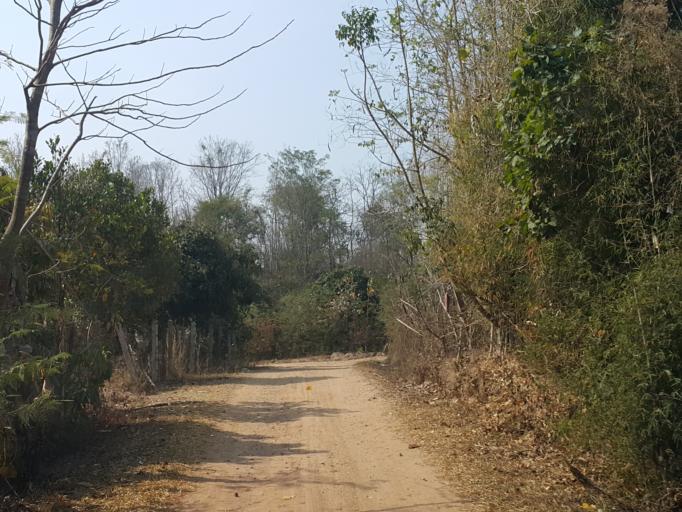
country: TH
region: Chiang Mai
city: Hang Dong
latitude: 18.7271
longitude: 98.8531
